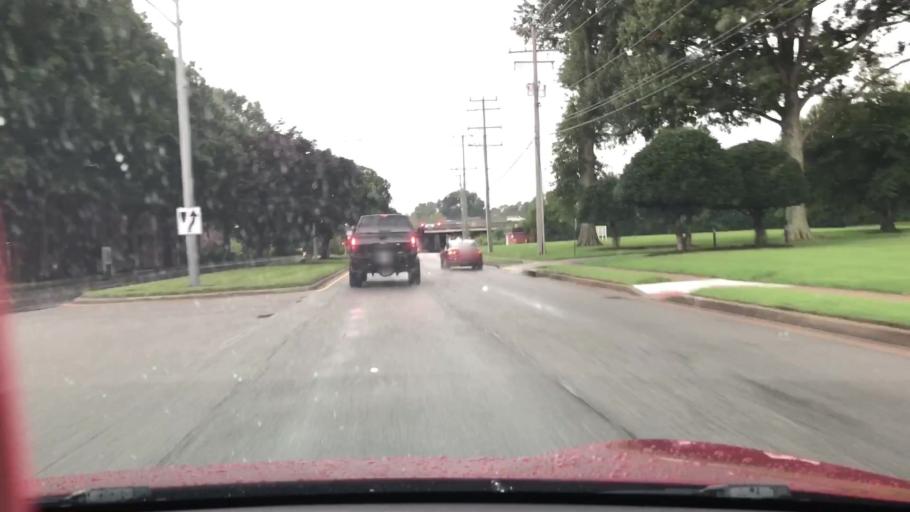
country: US
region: Virginia
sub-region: City of Chesapeake
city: Chesapeake
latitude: 36.8480
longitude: -76.1911
